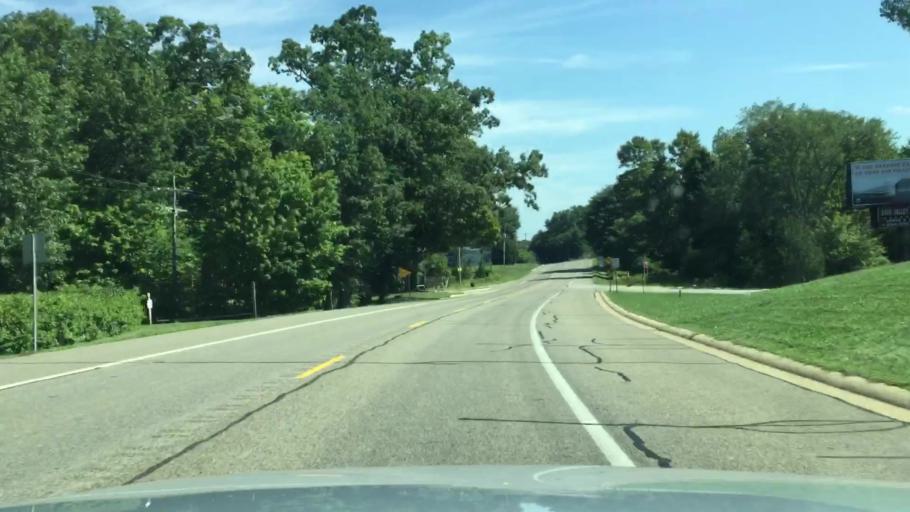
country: US
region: Michigan
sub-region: Jackson County
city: Brooklyn
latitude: 42.0519
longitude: -84.2680
